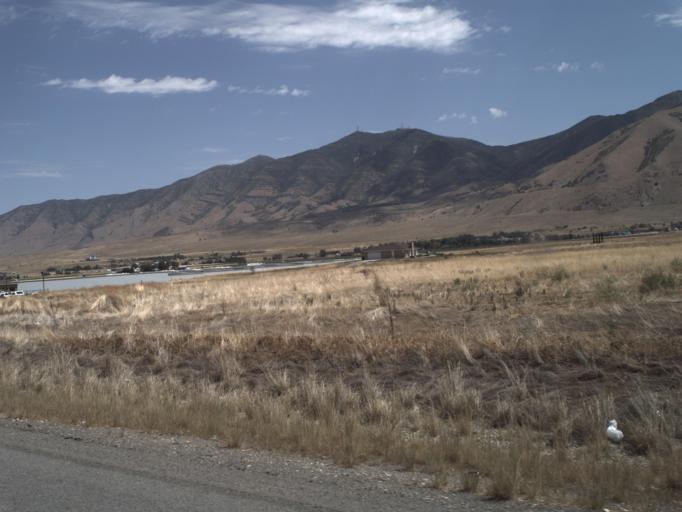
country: US
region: Utah
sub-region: Tooele County
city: Erda
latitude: 40.5883
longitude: -112.2939
